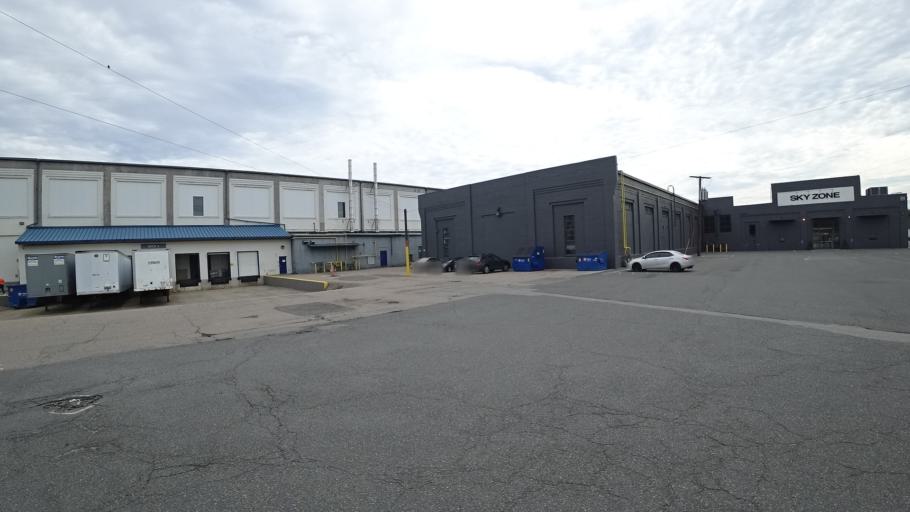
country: US
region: Massachusetts
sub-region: Norfolk County
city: Dedham
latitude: 42.2349
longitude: -71.1413
